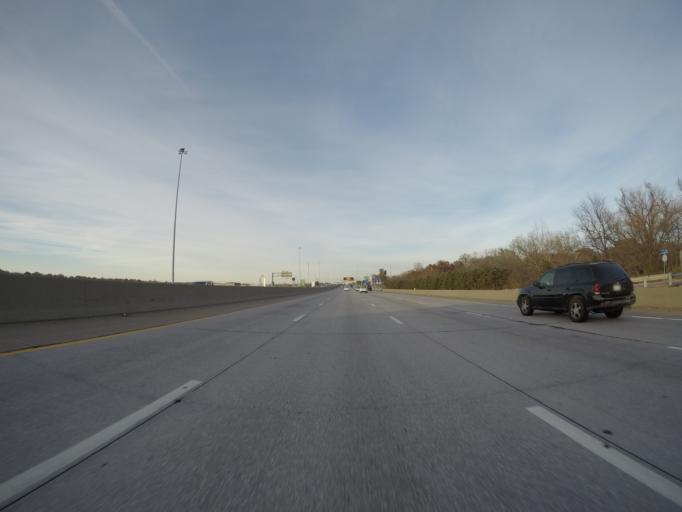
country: US
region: Kansas
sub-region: Johnson County
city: Merriam
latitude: 39.0011
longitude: -94.6946
